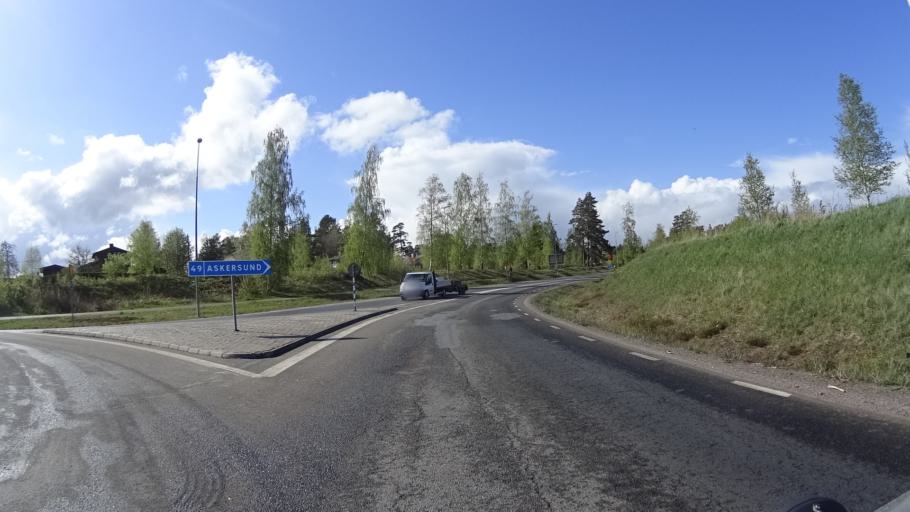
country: SE
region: Vaestra Goetaland
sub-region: Karlsborgs Kommun
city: Karlsborg
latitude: 58.5459
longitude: 14.5012
